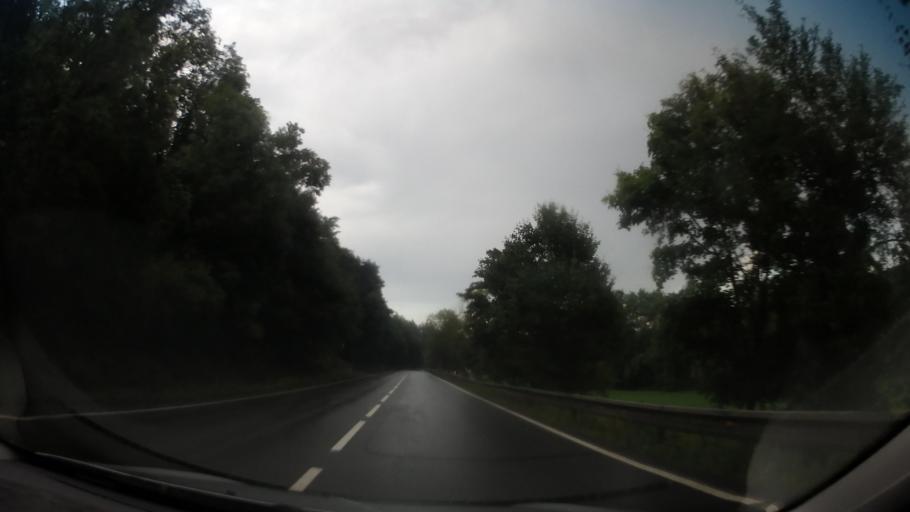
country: CZ
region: Olomoucky
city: Bila Lhota
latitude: 49.7041
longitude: 16.9928
